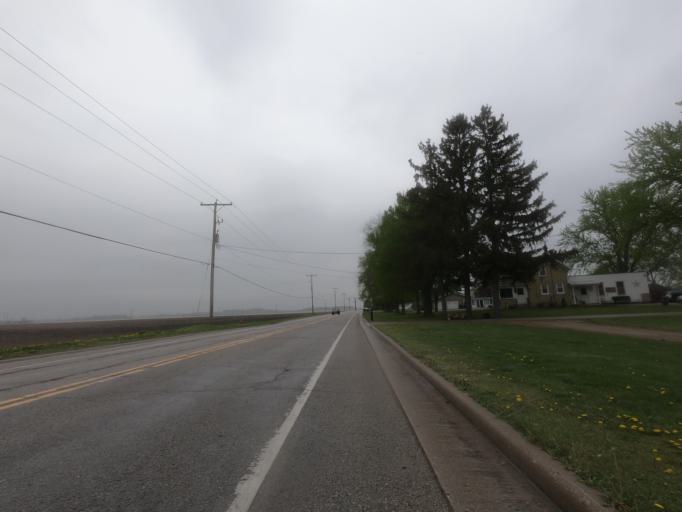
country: US
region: Wisconsin
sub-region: Jefferson County
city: Jefferson
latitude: 43.0185
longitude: -88.8176
